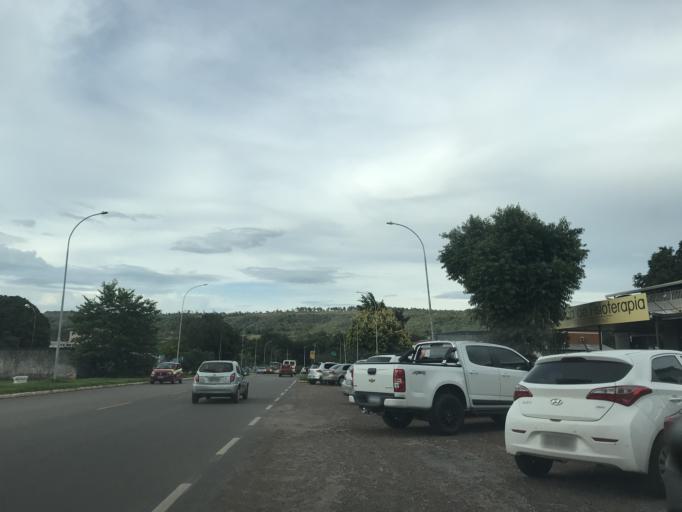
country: BR
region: Federal District
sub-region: Brasilia
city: Brasilia
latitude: -15.6416
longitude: -47.8020
